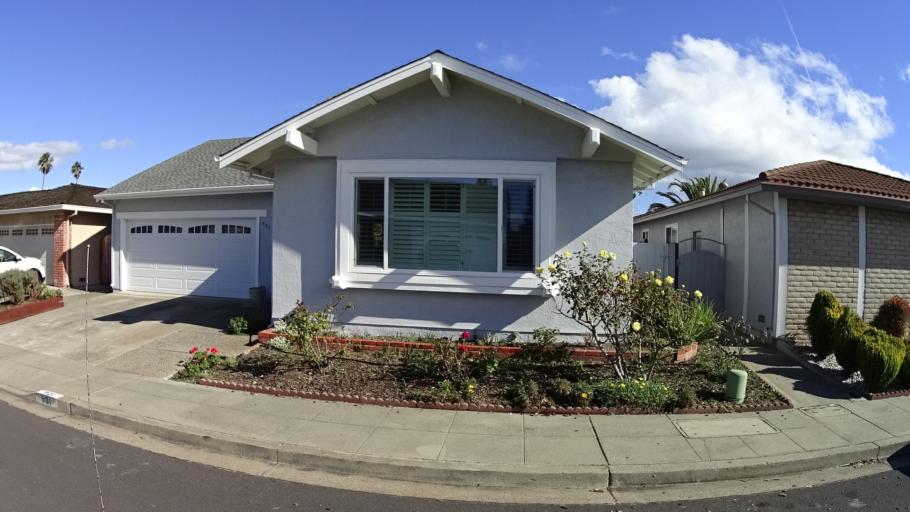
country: US
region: California
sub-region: San Mateo County
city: Foster City
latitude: 37.5563
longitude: -122.2499
